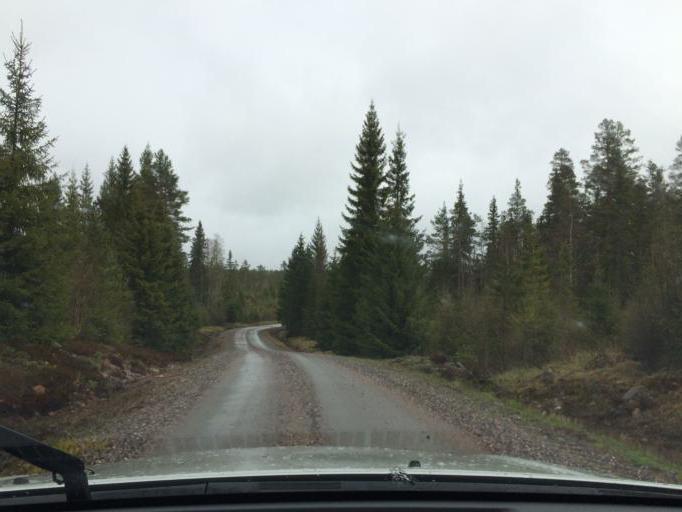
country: SE
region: OErebro
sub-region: Hallefors Kommun
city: Haellefors
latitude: 60.0336
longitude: 14.5378
